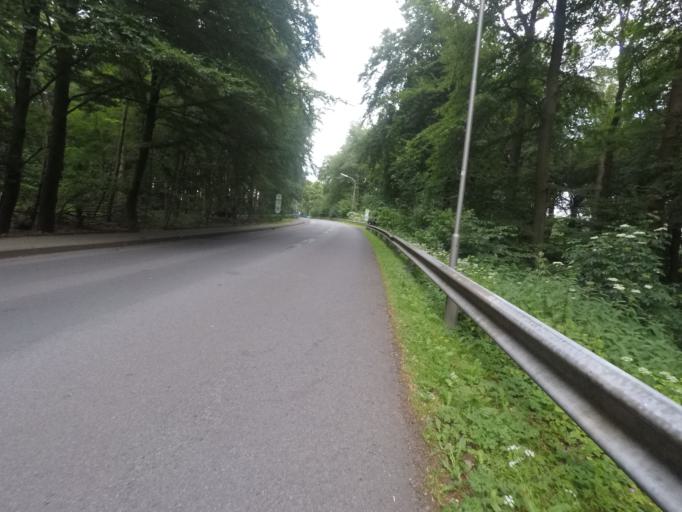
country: DE
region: North Rhine-Westphalia
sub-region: Regierungsbezirk Detmold
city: Hiddenhausen
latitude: 52.1762
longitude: 8.6003
